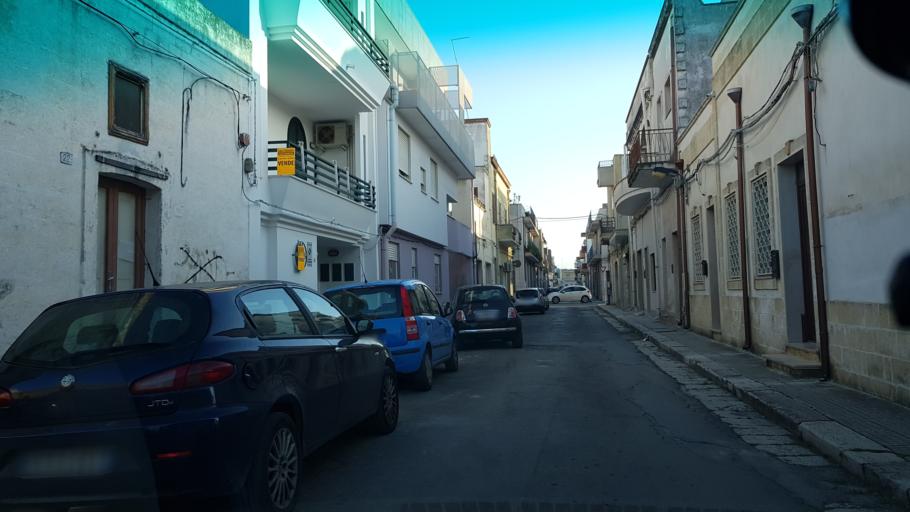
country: IT
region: Apulia
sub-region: Provincia di Brindisi
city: Mesagne
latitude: 40.5610
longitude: 17.8041
